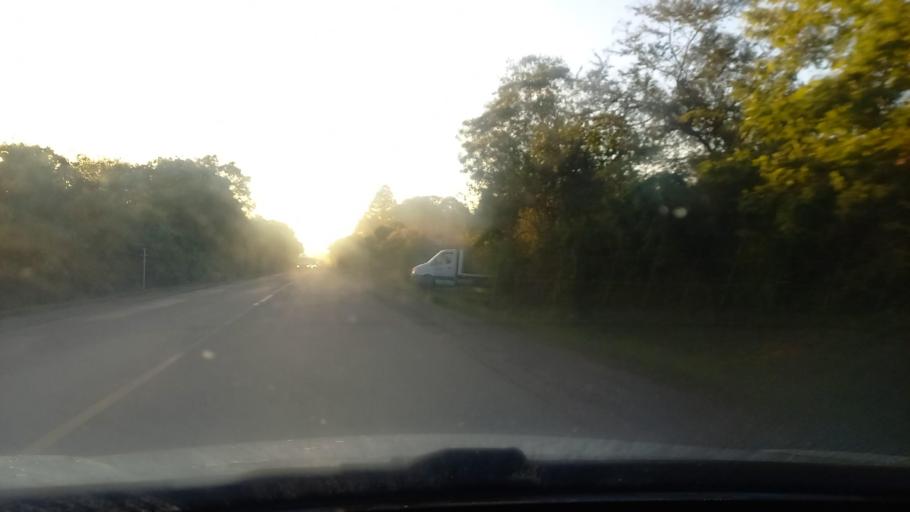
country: BR
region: Rio Grande do Sul
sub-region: Candelaria
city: Candelaria
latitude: -29.6808
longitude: -52.8369
